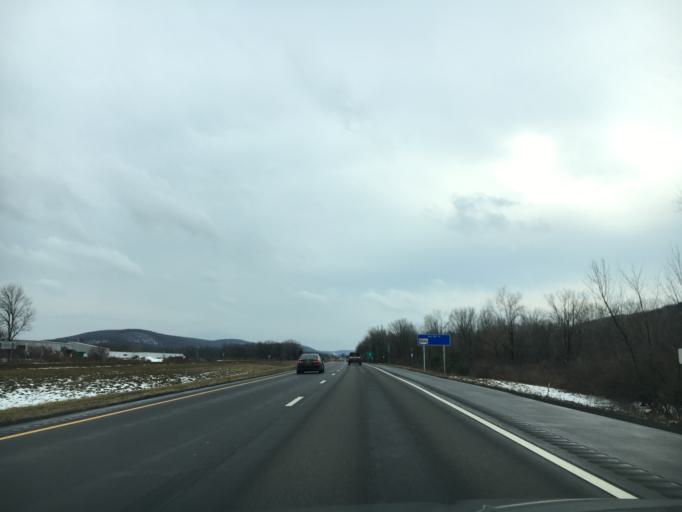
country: US
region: New York
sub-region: Cortland County
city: Homer
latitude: 42.7589
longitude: -76.1344
